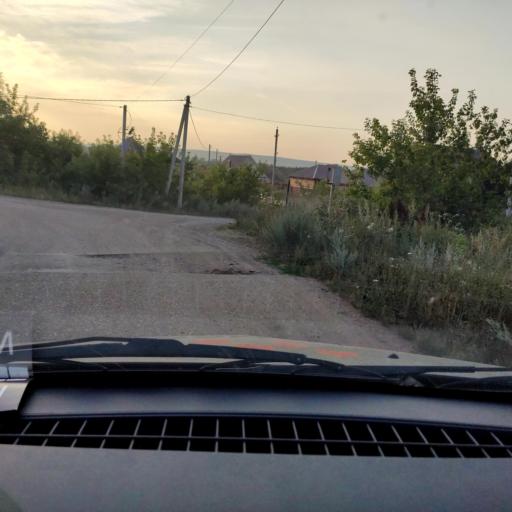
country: RU
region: Bashkortostan
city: Avdon
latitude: 54.5896
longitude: 55.6765
